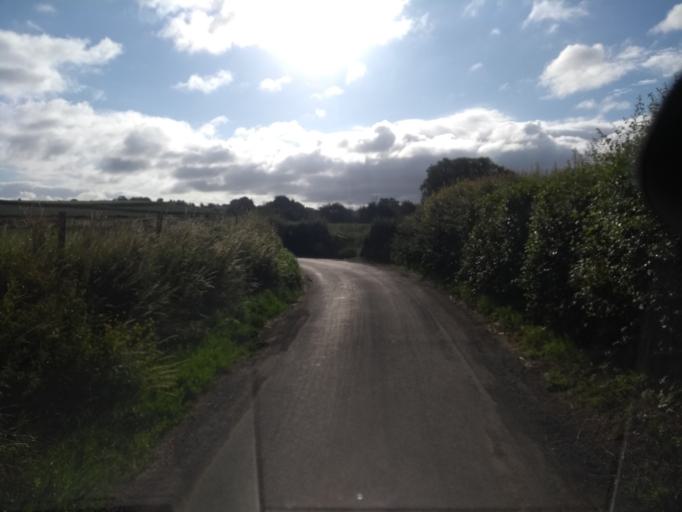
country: GB
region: England
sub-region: Somerset
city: Creech Saint Michael
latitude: 51.0209
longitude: -3.0084
